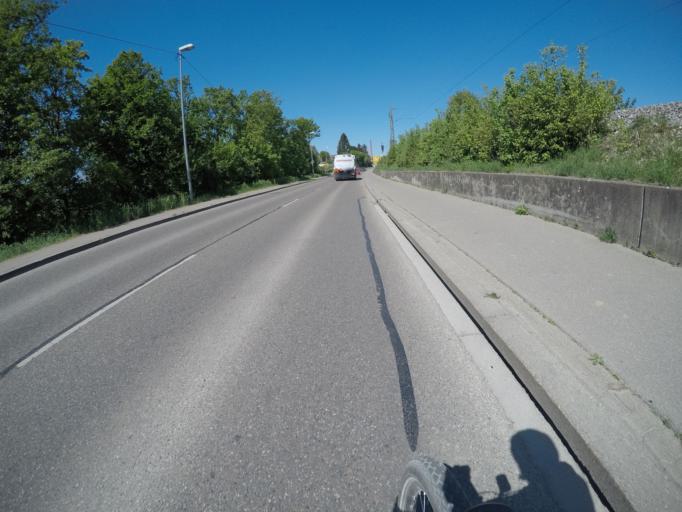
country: DE
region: Baden-Wuerttemberg
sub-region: Regierungsbezirk Stuttgart
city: Waiblingen
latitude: 48.8180
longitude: 9.3146
